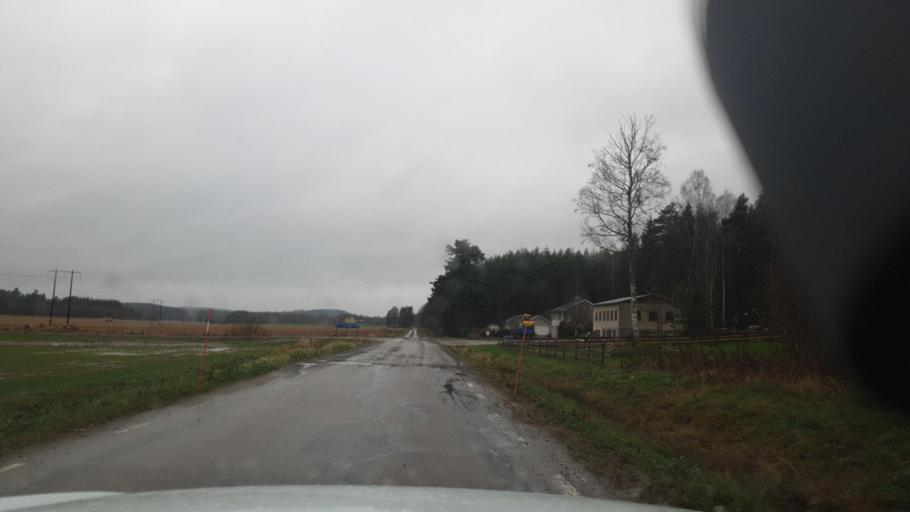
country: SE
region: Vaermland
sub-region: Arvika Kommun
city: Arvika
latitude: 59.4882
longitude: 12.7476
